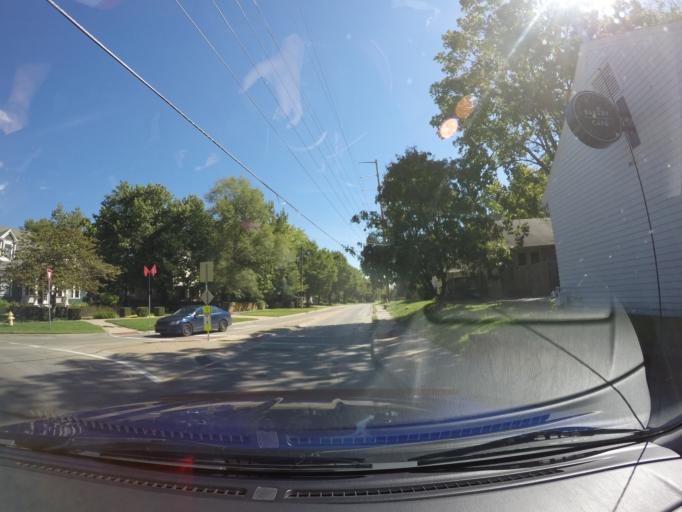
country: US
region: Kansas
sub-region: Douglas County
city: Lawrence
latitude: 38.9500
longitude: -95.2327
